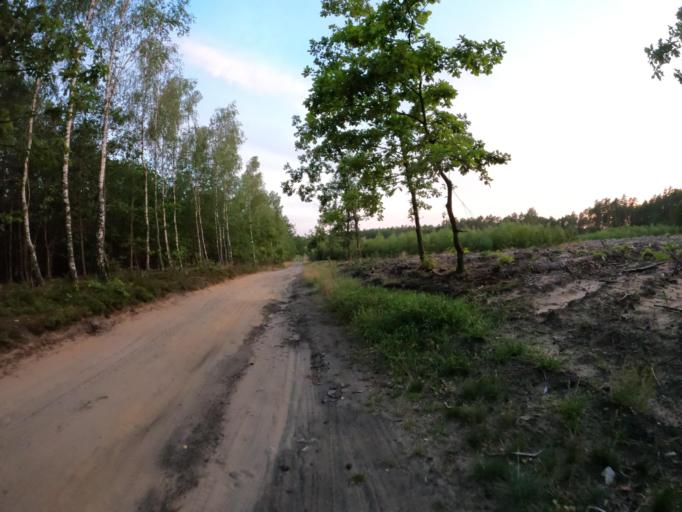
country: PL
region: West Pomeranian Voivodeship
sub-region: Powiat koszalinski
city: Sianow
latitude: 54.0811
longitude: 16.3991
